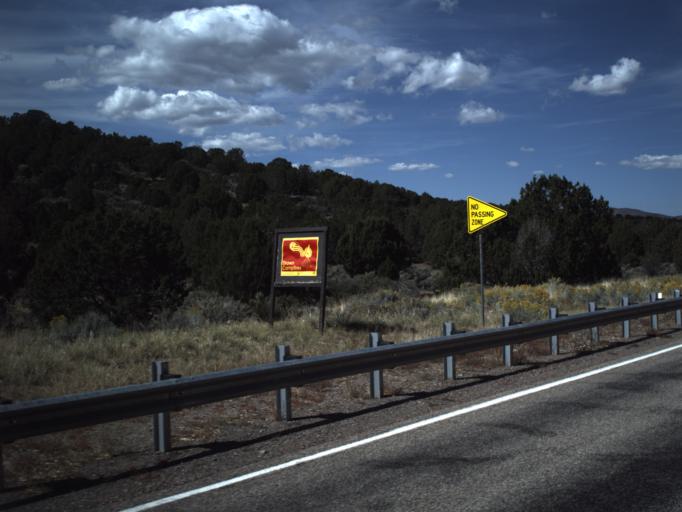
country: US
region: Utah
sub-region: Washington County
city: Enterprise
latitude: 37.5491
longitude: -113.6859
